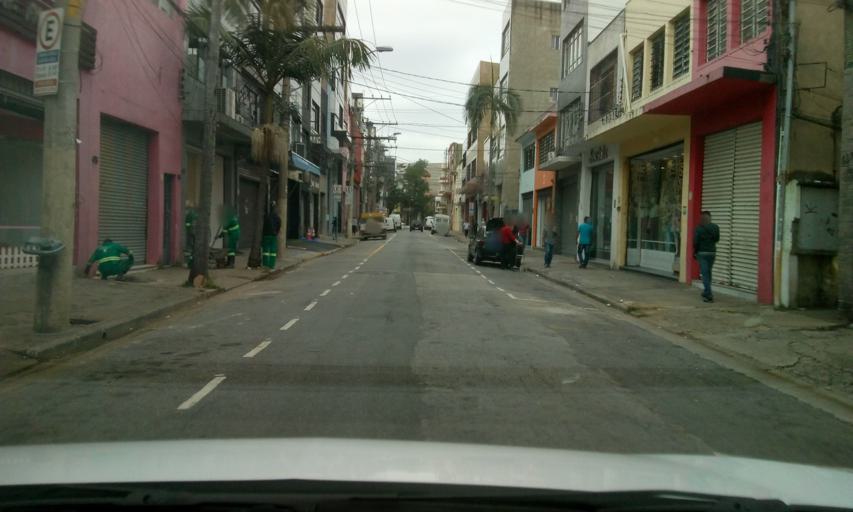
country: BR
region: Sao Paulo
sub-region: Sao Paulo
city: Sao Paulo
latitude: -23.5337
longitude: -46.6163
